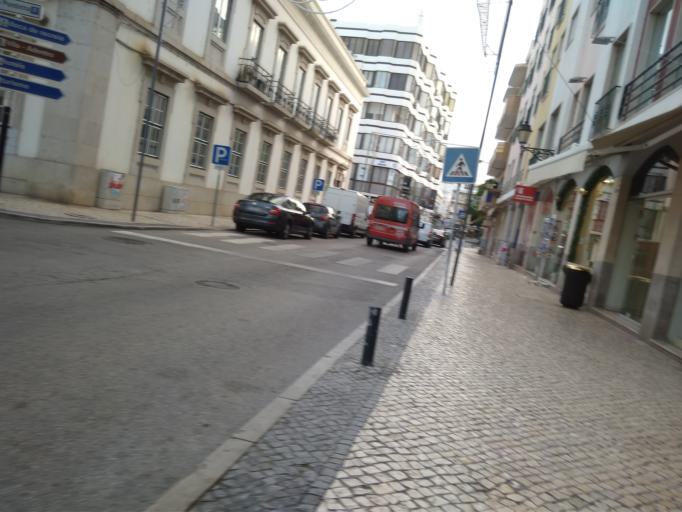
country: PT
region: Faro
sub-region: Faro
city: Faro
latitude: 37.0163
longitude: -7.9316
